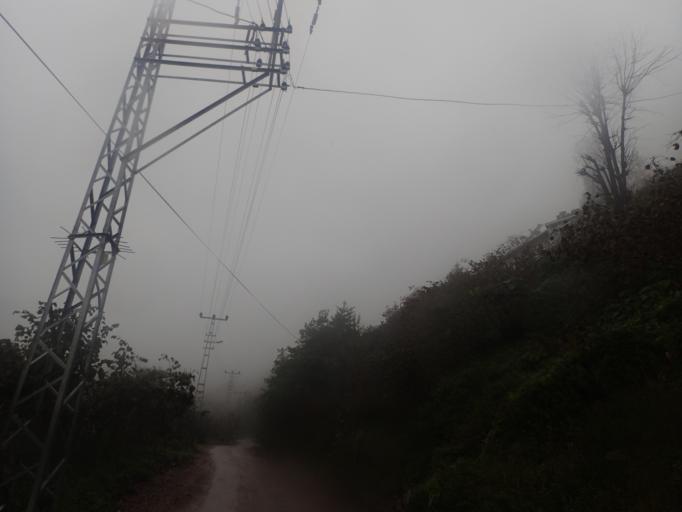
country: TR
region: Ordu
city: Persembe
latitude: 41.0395
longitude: 37.7225
